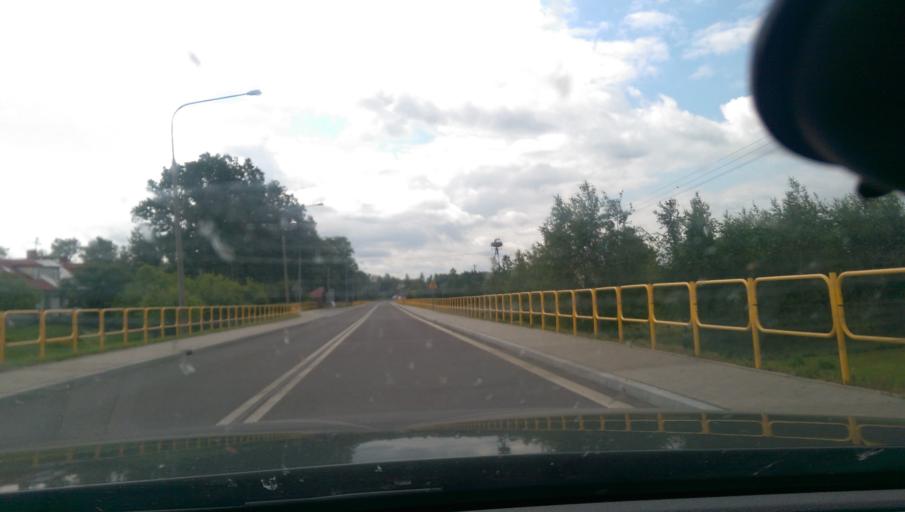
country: PL
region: Warmian-Masurian Voivodeship
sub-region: Powiat olecki
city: Kowale Oleckie
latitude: 54.2116
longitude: 22.4123
